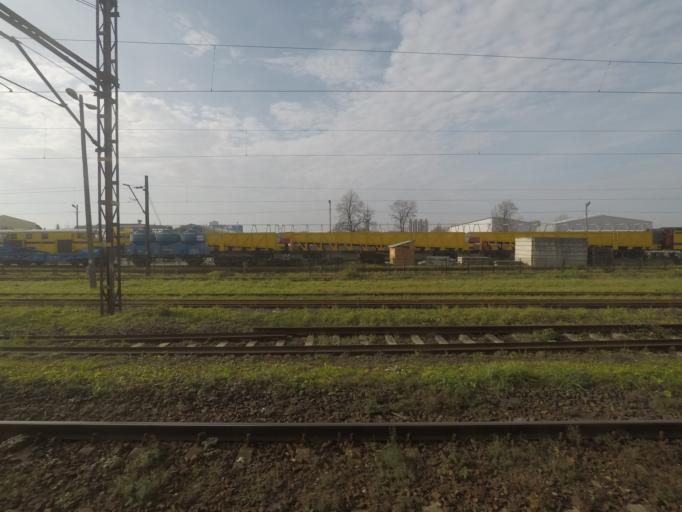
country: PL
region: Subcarpathian Voivodeship
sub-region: Rzeszow
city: Rzeszow
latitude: 50.0508
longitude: 21.9945
